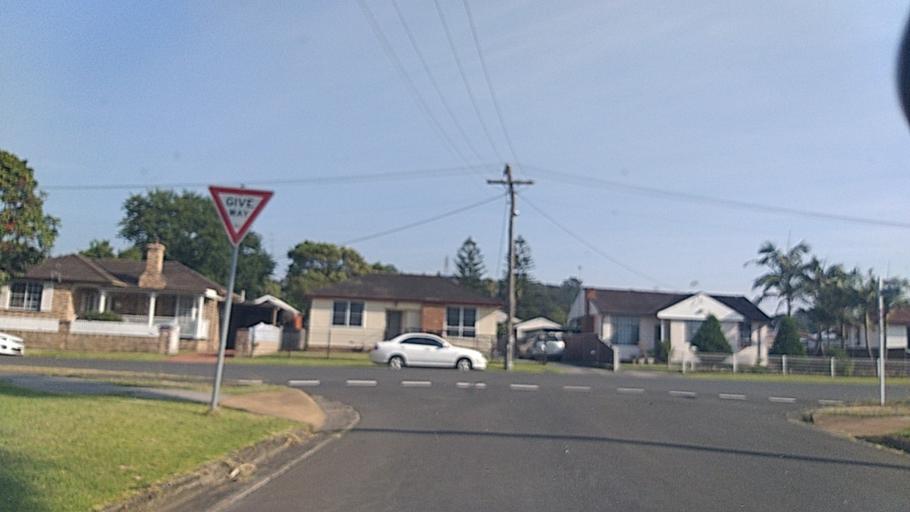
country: AU
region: New South Wales
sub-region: Wollongong
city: Berkeley
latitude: -34.4793
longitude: 150.8498
